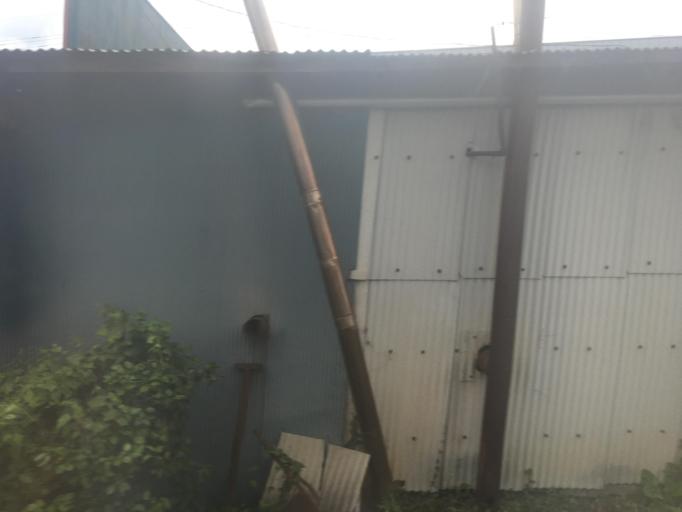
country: JP
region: Saitama
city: Kodamacho-kodamaminami
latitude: 36.1091
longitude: 139.1106
